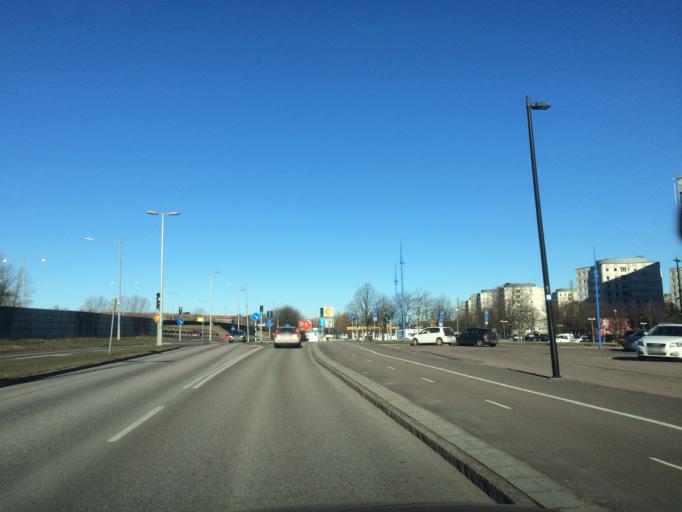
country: SE
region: Vaestra Goetaland
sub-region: Goteborg
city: Majorna
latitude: 57.6512
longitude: 11.9085
